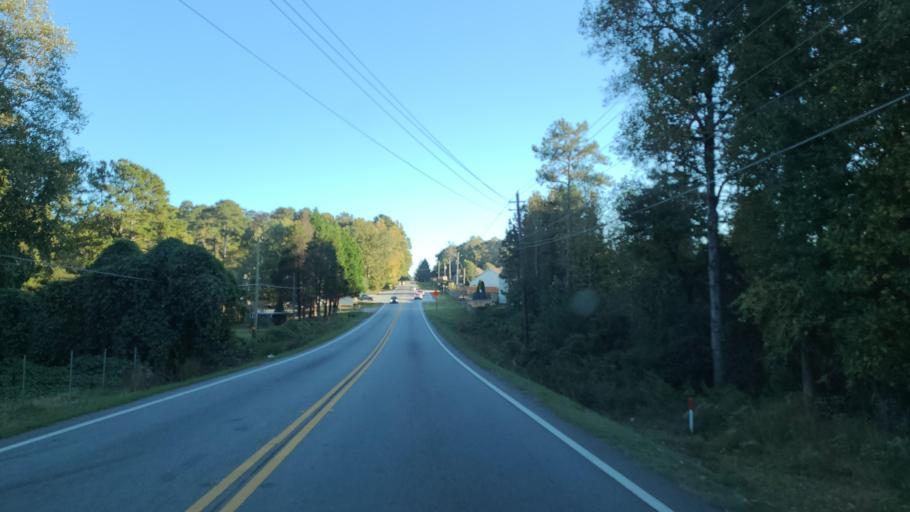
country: US
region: Georgia
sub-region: Clayton County
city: Lake City
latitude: 33.5994
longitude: -84.2981
